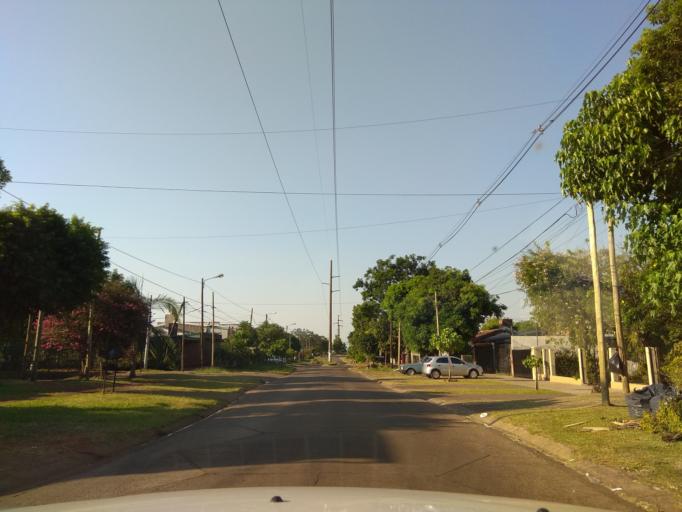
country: AR
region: Misiones
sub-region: Departamento de Capital
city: Posadas
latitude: -27.3688
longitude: -55.9129
